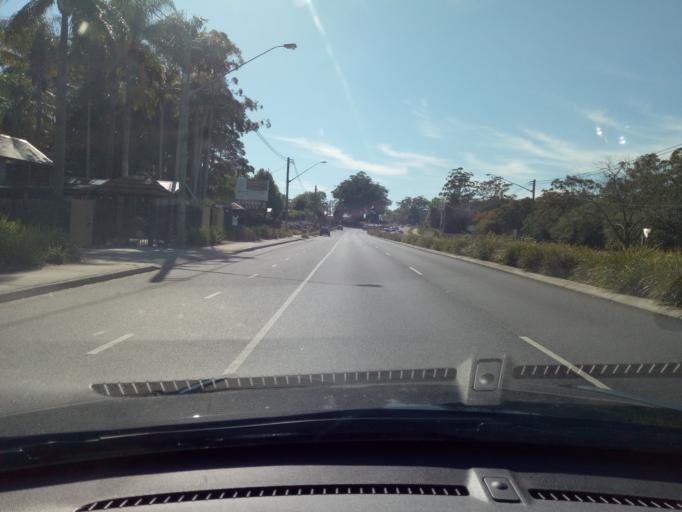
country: AU
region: New South Wales
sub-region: Gosford Shire
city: Erina
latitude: -33.4254
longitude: 151.4016
